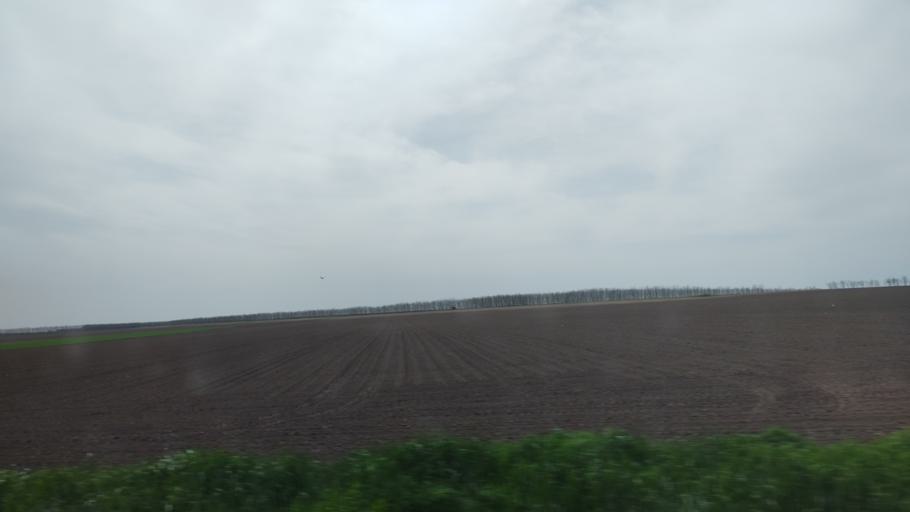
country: RO
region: Constanta
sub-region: Comuna Deleni
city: Pietreni
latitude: 44.0818
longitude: 28.1149
